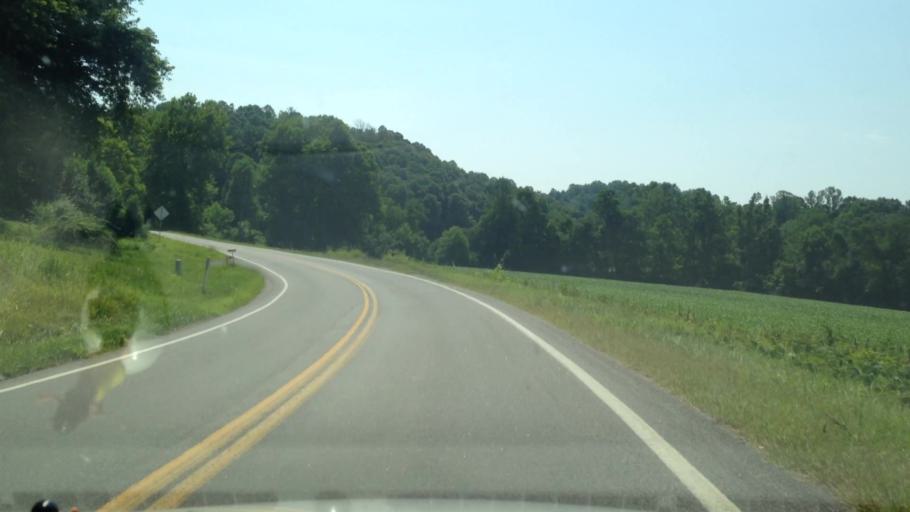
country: US
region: Virginia
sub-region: Patrick County
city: Stuart
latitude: 36.5771
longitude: -80.3796
